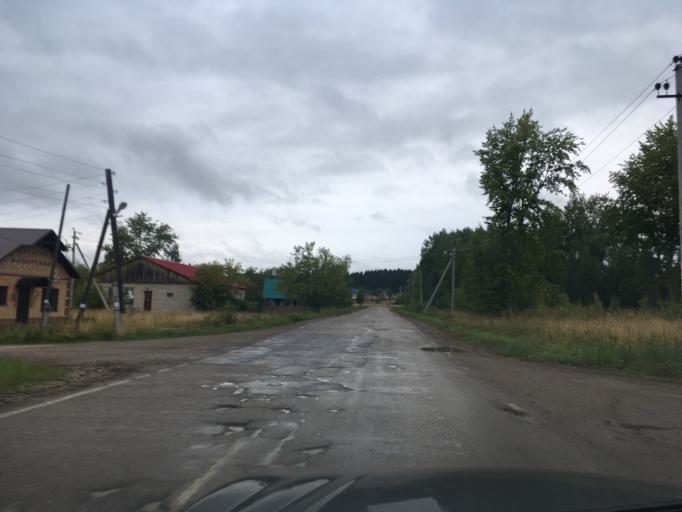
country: RU
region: Perm
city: Verkhnechusovskiye Gorodki
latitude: 58.1727
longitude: 57.1088
